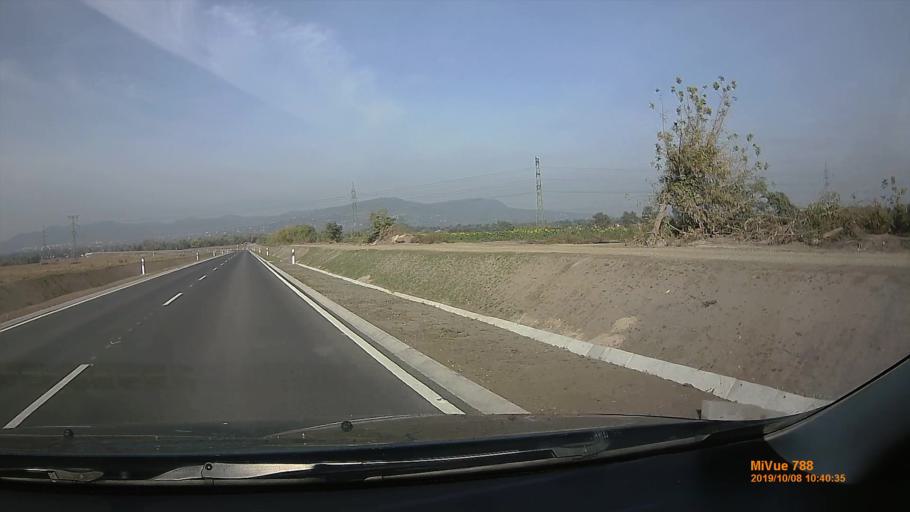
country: HU
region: Pest
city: God
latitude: 47.6623
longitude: 19.1430
